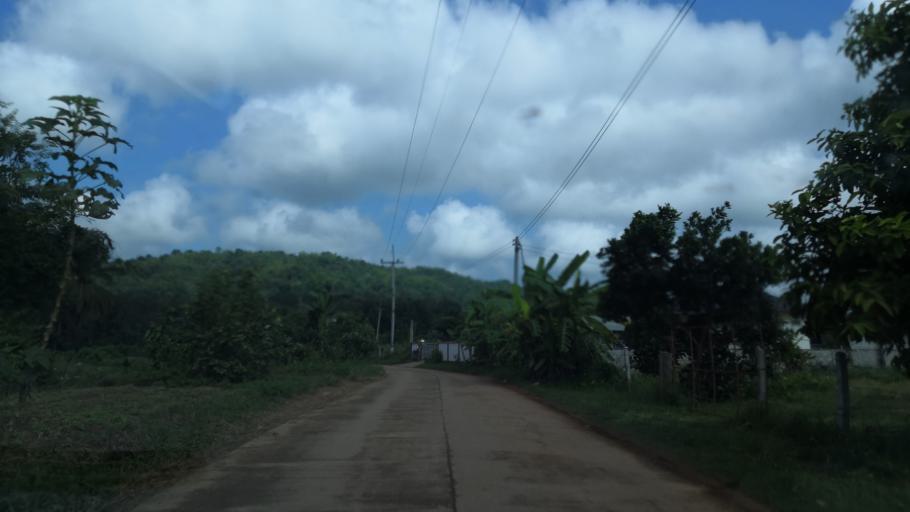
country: TH
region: Chiang Rai
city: Wiang Chiang Rung
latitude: 20.0152
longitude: 100.0406
